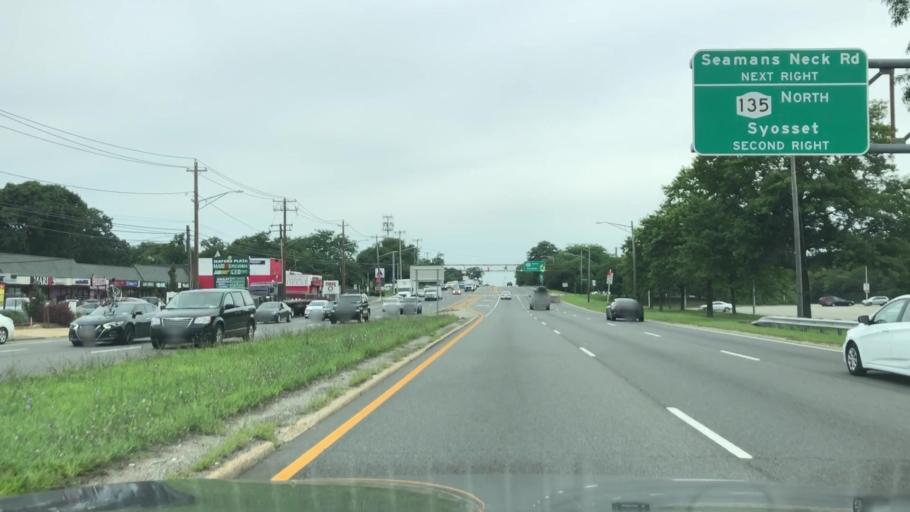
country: US
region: New York
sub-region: Nassau County
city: Seaford
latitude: 40.6747
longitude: -73.4894
